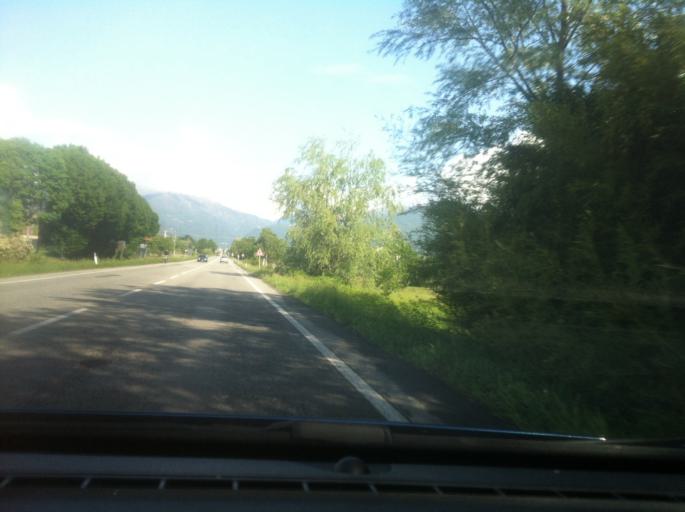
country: IT
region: Piedmont
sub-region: Provincia di Torino
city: Salassa
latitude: 45.3600
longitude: 7.6916
